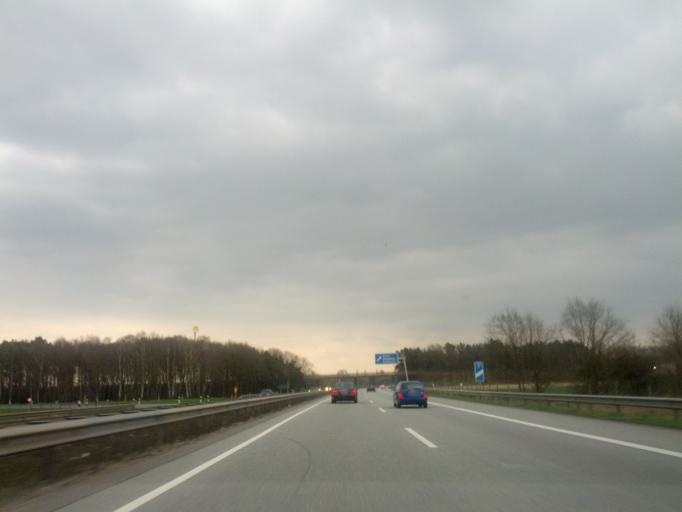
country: DE
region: Lower Saxony
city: Achim
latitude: 53.0198
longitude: 9.0607
